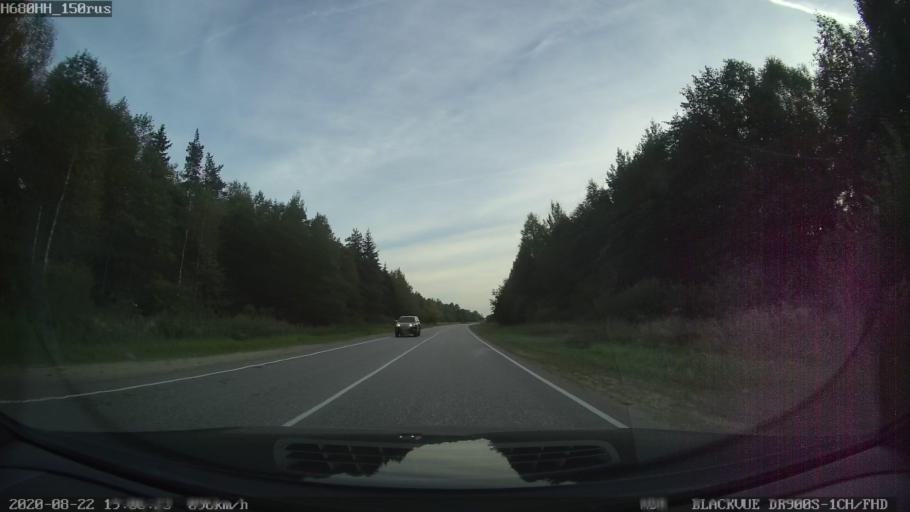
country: RU
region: Tverskaya
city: Sakharovo
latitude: 57.0641
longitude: 36.1051
